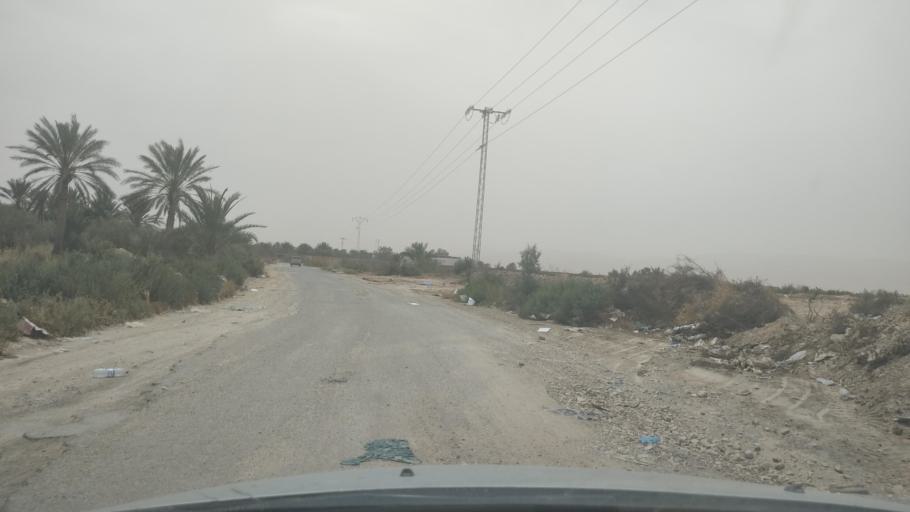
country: TN
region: Gafsa
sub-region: Gafsa Municipality
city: Gafsa
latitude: 34.3251
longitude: 8.9513
